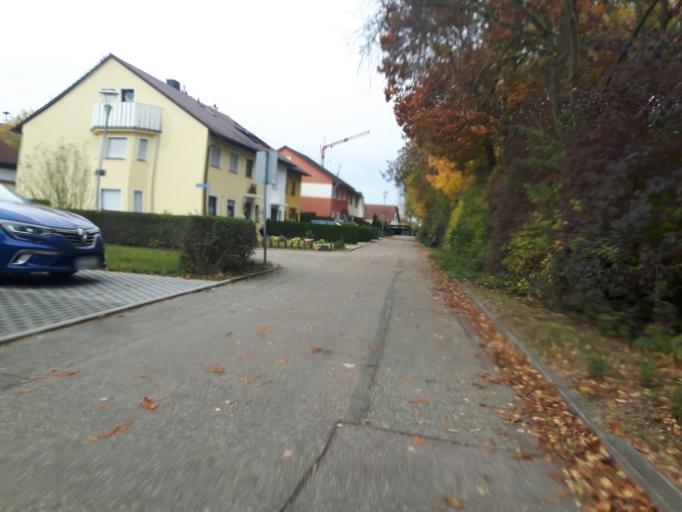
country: DE
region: Baden-Wuerttemberg
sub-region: Regierungsbezirk Stuttgart
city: Gemmingen
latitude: 49.1571
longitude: 8.9760
